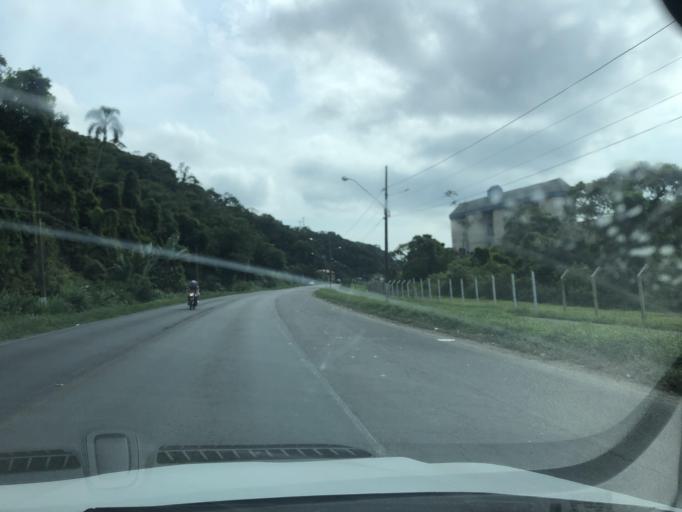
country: BR
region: Santa Catarina
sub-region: Sao Francisco Do Sul
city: Sao Francisco do Sul
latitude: -26.2381
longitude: -48.6303
